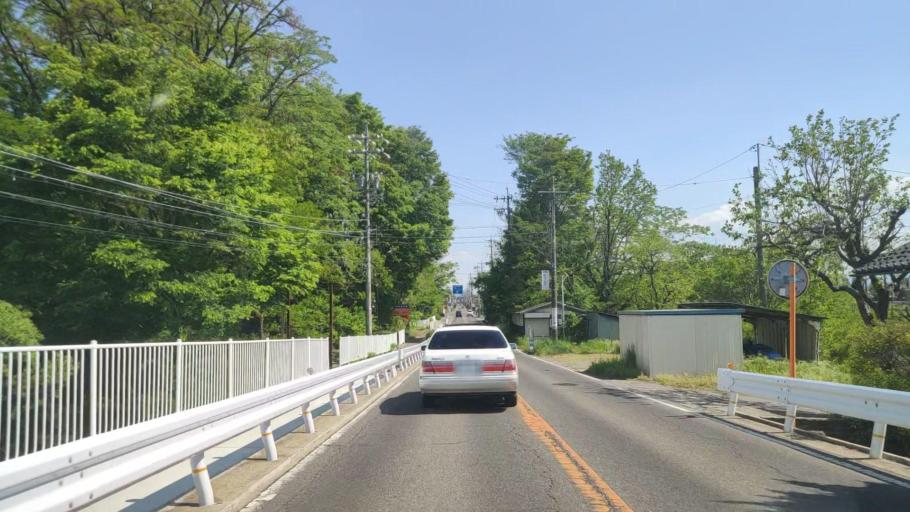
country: JP
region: Nagano
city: Hotaka
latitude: 36.3501
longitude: 137.8827
